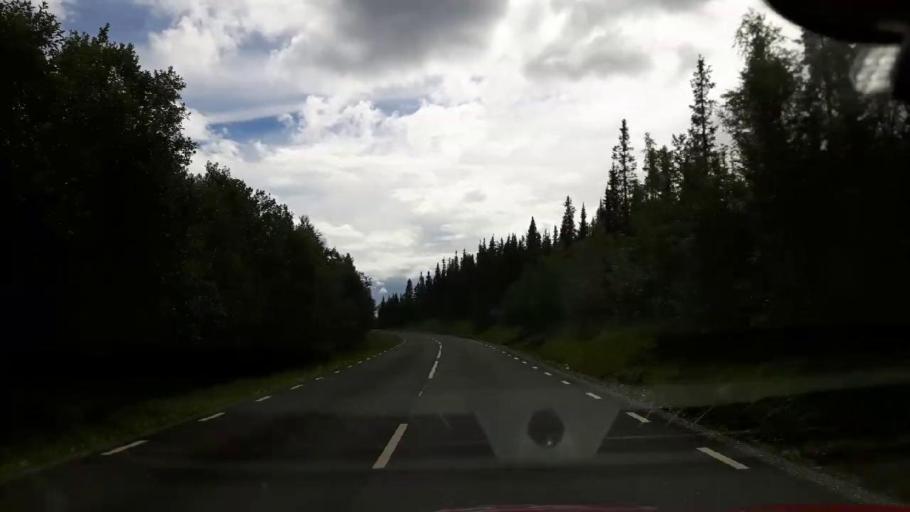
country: NO
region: Nord-Trondelag
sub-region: Royrvik
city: Royrvik
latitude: 64.8091
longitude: 14.0680
